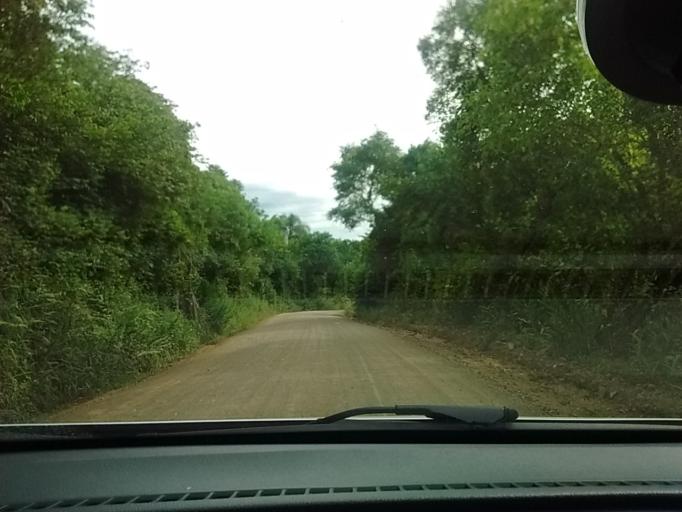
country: BR
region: Rio Grande do Sul
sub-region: Tres Coroas
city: Tres Coroas
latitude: -29.4492
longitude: -50.7595
